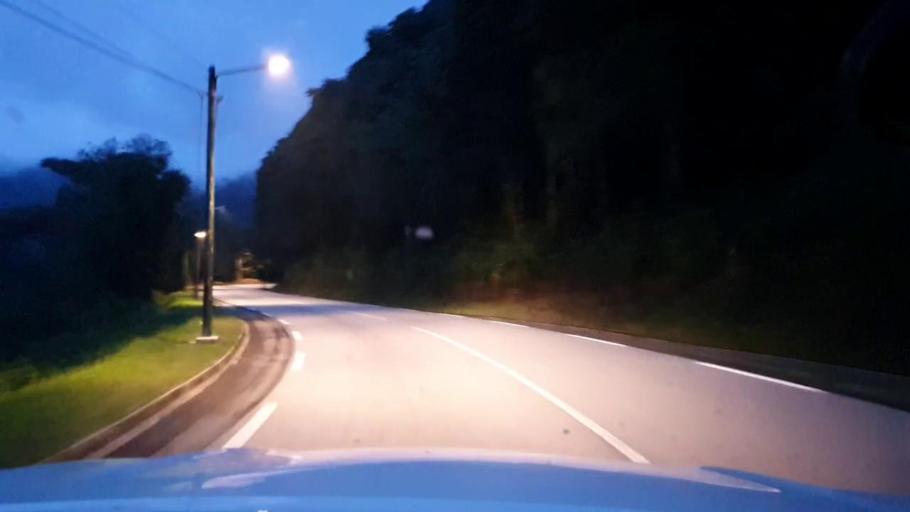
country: RW
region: Southern Province
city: Nzega
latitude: -2.5326
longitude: 29.3897
